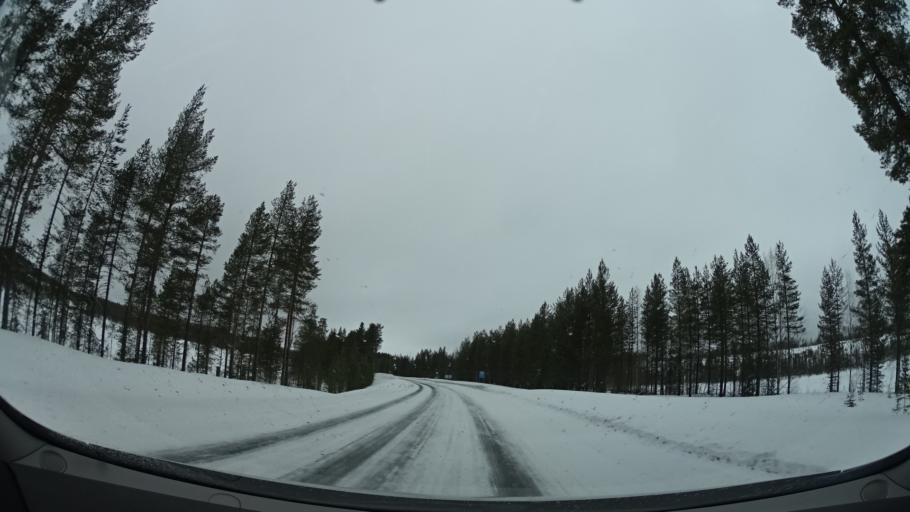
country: SE
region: Vaesterbotten
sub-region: Mala Kommun
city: Mala
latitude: 65.1525
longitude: 18.8040
